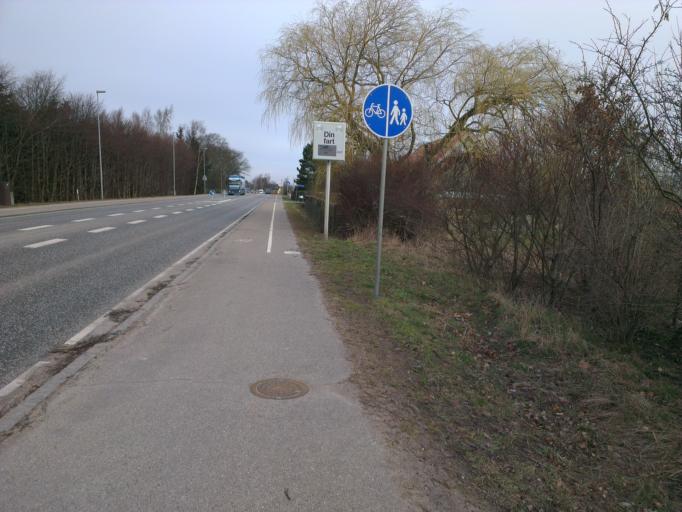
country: DK
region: Capital Region
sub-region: Frederikssund Kommune
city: Jaegerspris
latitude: 55.8027
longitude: 11.9812
